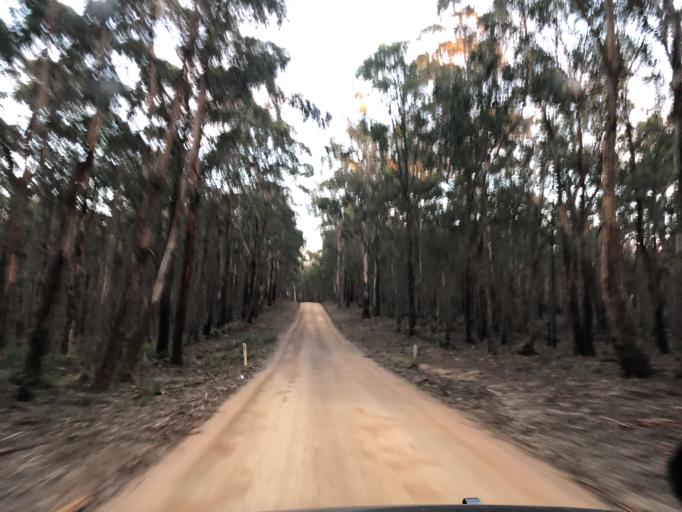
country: AU
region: Victoria
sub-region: Moorabool
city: Bacchus Marsh
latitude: -37.4821
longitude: 144.4361
